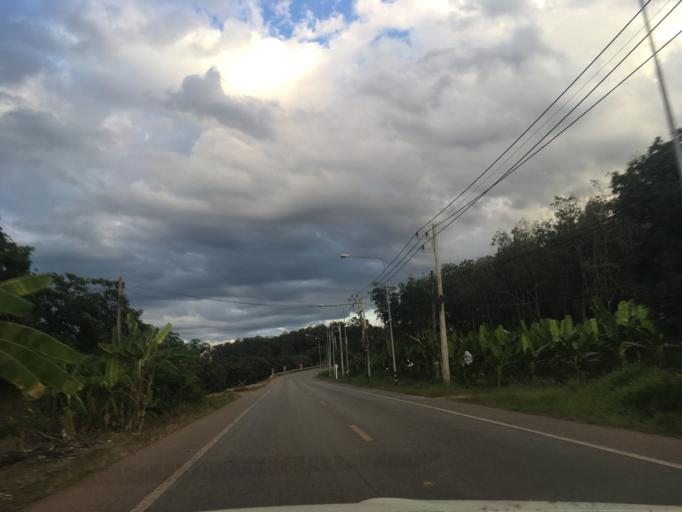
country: TH
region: Chanthaburi
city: Na Yai Am
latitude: 12.6830
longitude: 101.8421
